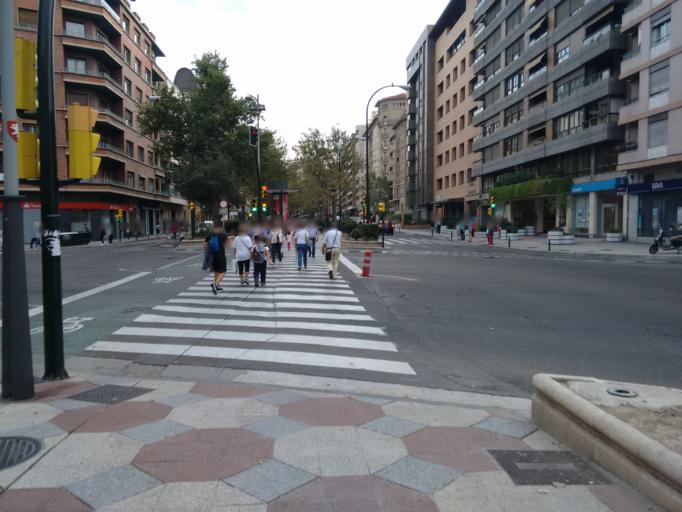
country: ES
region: Aragon
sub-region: Provincia de Zaragoza
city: Zaragoza
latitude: 41.6423
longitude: -0.8863
